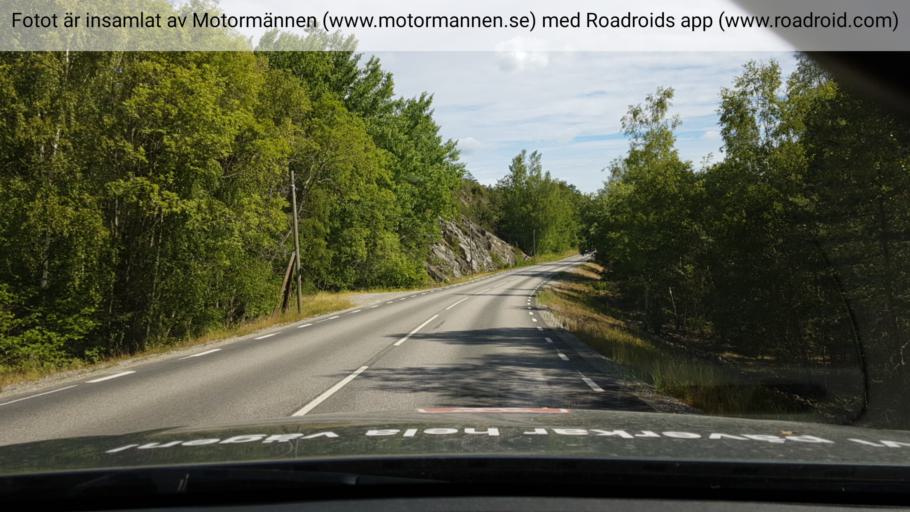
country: SE
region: Stockholm
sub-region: Nynashamns Kommun
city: Nynashamn
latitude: 58.9572
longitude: 18.0179
